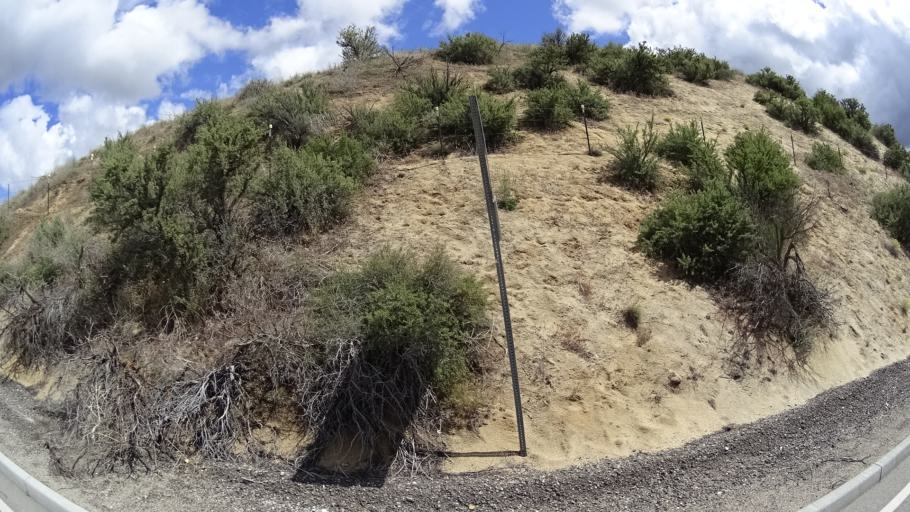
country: US
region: Idaho
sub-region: Ada County
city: Boise
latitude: 43.6625
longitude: -116.1912
